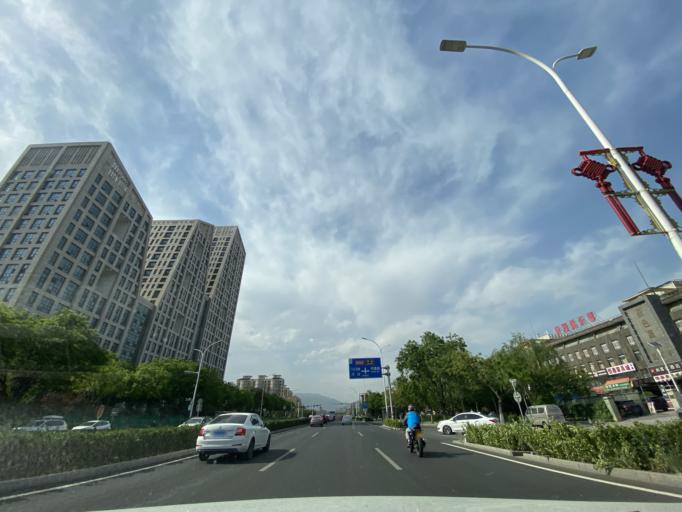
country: CN
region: Beijing
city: Dayu
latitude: 39.9417
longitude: 116.1016
